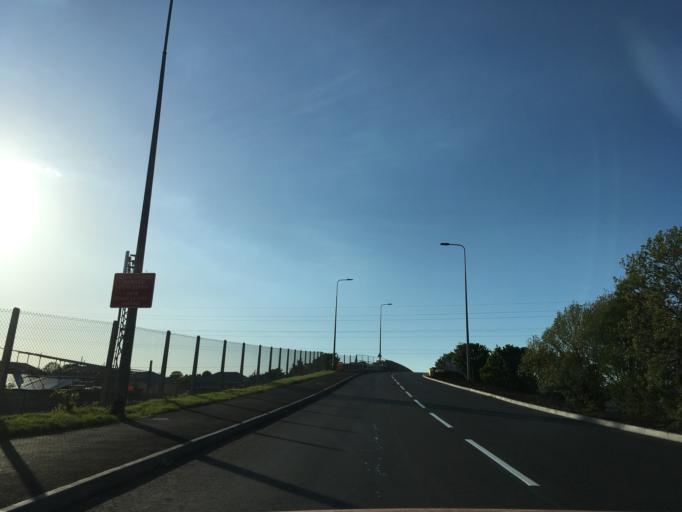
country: GB
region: Wales
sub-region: Newport
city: Marshfield
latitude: 51.5022
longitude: -3.1199
